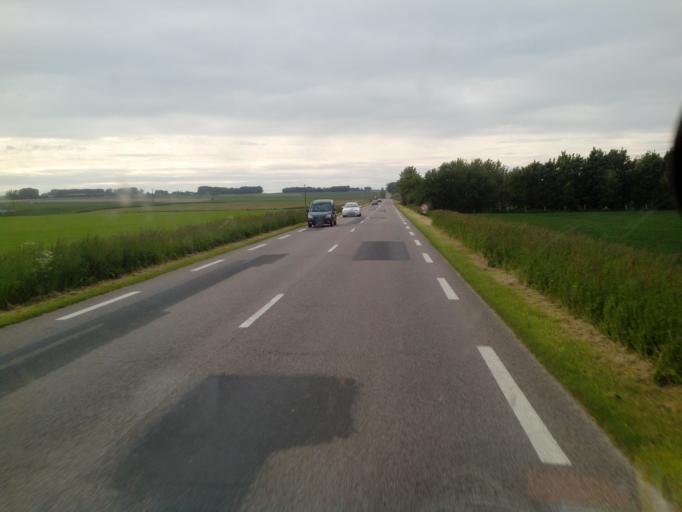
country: FR
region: Haute-Normandie
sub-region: Departement de la Seine-Maritime
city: Fauville-en-Caux
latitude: 49.6736
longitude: 0.5700
